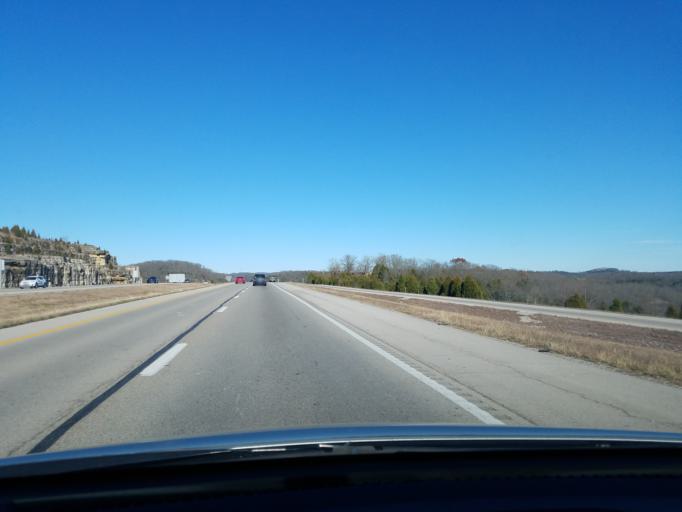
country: US
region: Missouri
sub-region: Taney County
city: Merriam Woods
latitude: 36.7505
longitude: -93.2226
